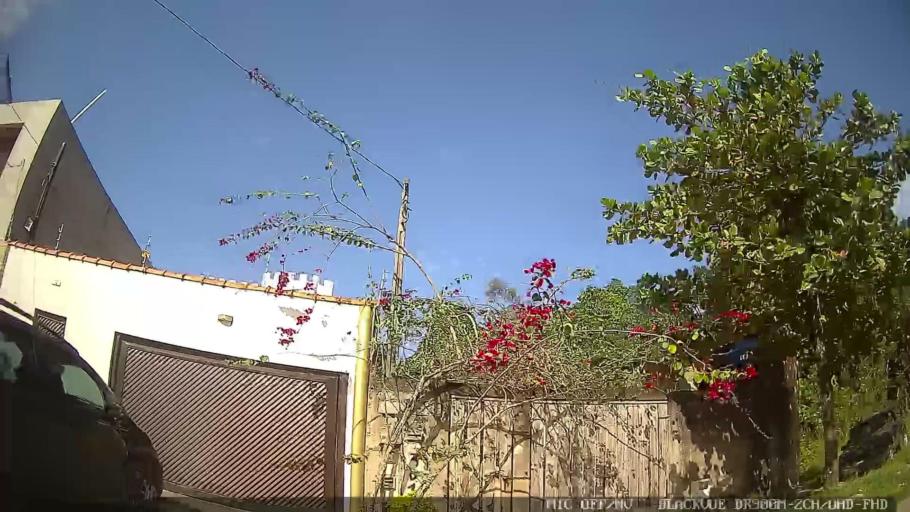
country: BR
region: Sao Paulo
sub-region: Guaruja
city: Guaruja
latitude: -23.9758
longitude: -46.2156
